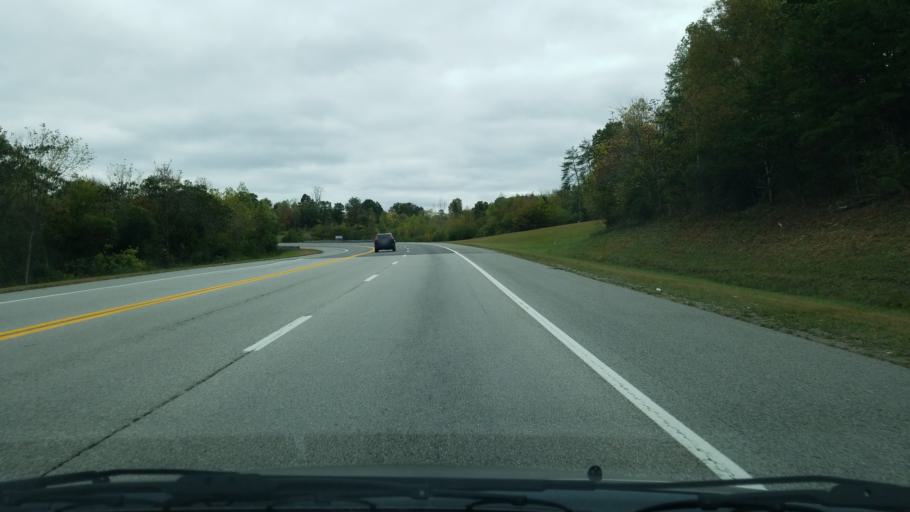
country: US
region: Tennessee
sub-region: Rhea County
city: Dayton
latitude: 35.4723
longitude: -85.0215
